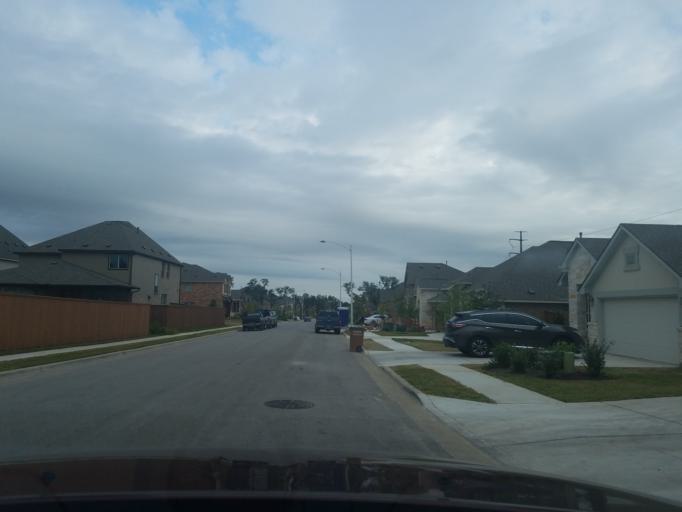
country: US
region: Texas
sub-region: Williamson County
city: Anderson Mill
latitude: 30.4833
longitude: -97.7886
